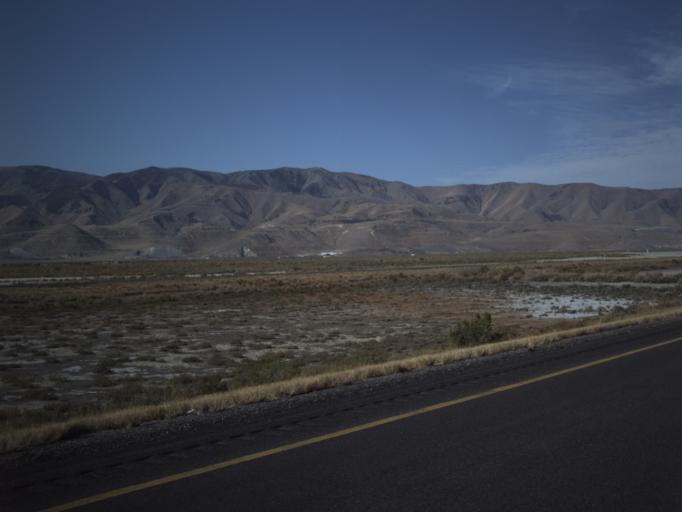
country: US
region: Utah
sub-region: Tooele County
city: Grantsville
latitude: 40.7027
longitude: -112.4973
